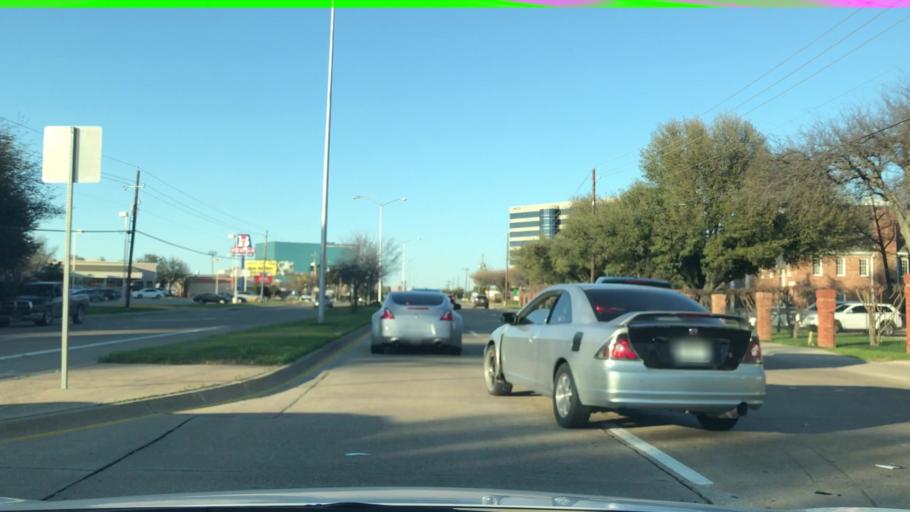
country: US
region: Texas
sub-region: Dallas County
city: Addison
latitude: 32.9939
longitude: -96.7998
